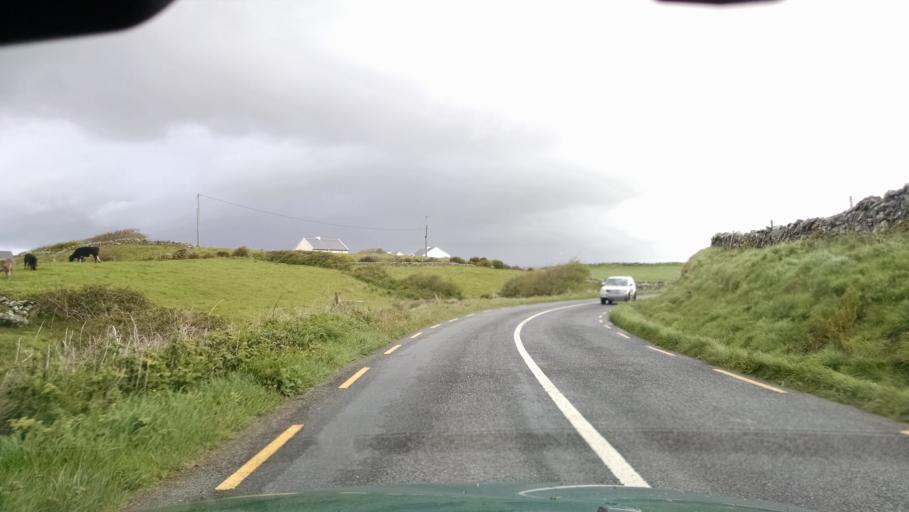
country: IE
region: Connaught
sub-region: County Galway
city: Bearna
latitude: 53.0101
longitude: -9.3481
